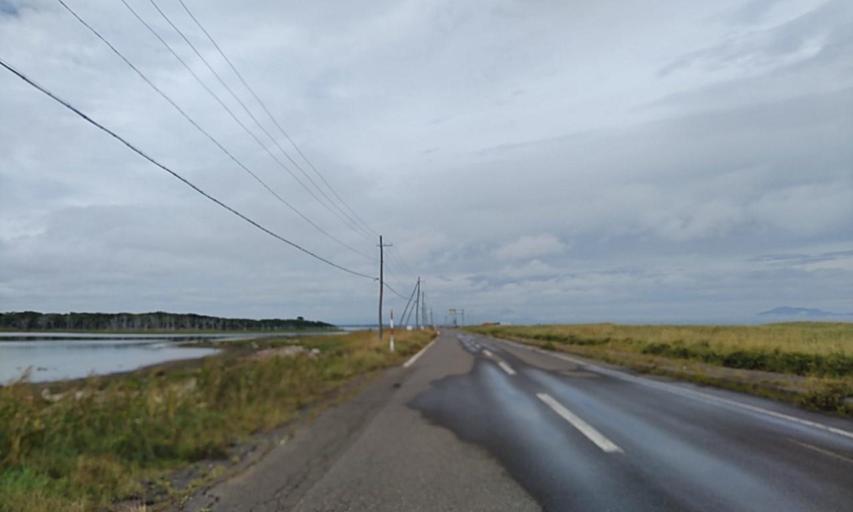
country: JP
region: Hokkaido
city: Shibetsu
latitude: 43.6087
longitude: 145.2765
